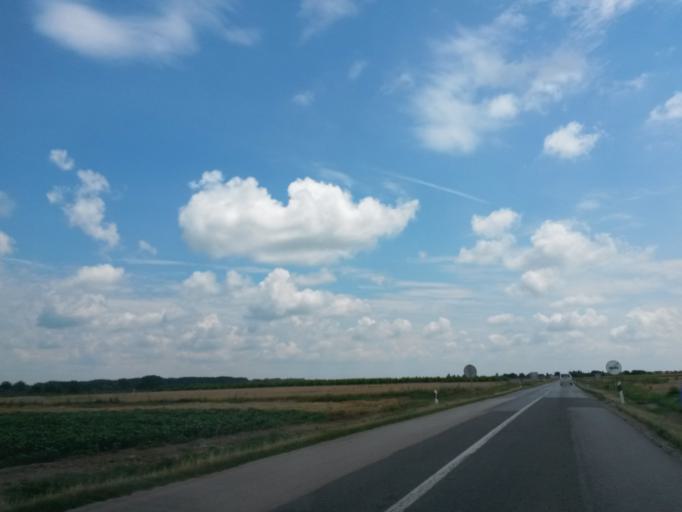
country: HR
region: Osjecko-Baranjska
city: Sarvas
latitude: 45.5335
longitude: 18.8161
